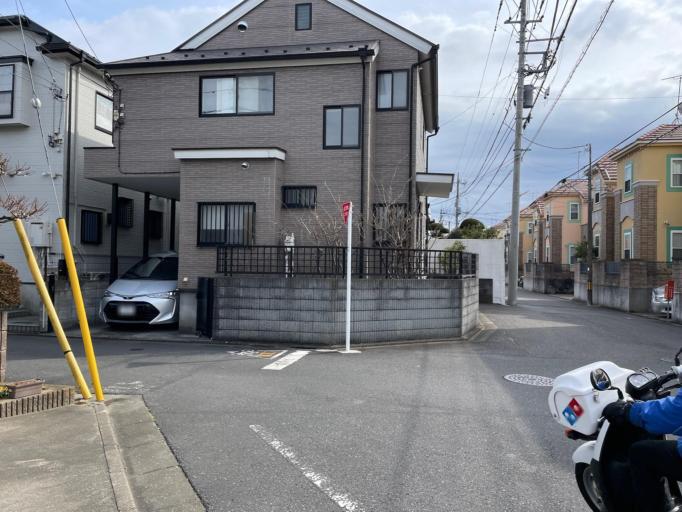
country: JP
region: Tokyo
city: Kokubunji
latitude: 35.6602
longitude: 139.4508
